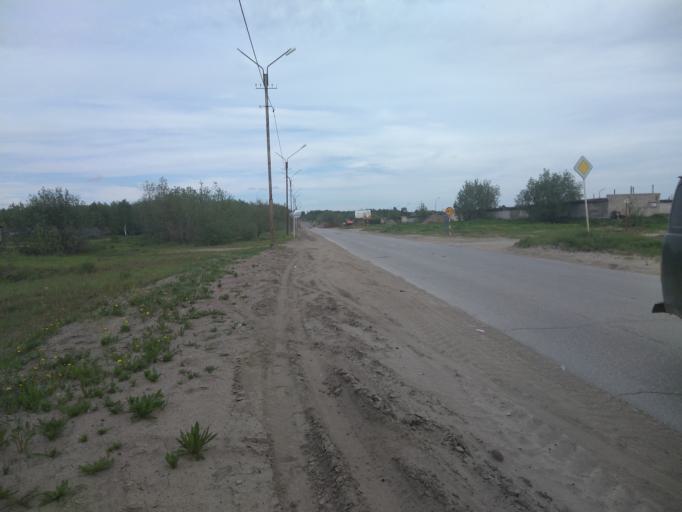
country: RU
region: Komi Republic
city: Pechora
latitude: 65.1431
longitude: 57.2469
